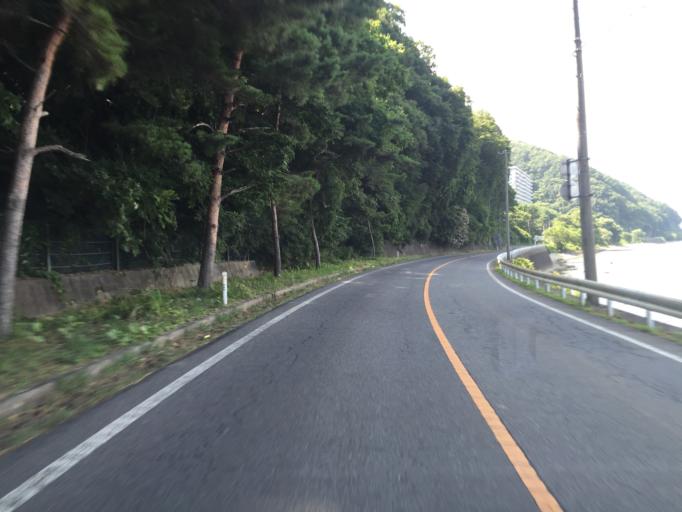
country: JP
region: Fukushima
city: Inawashiro
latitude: 37.4638
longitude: 140.1554
